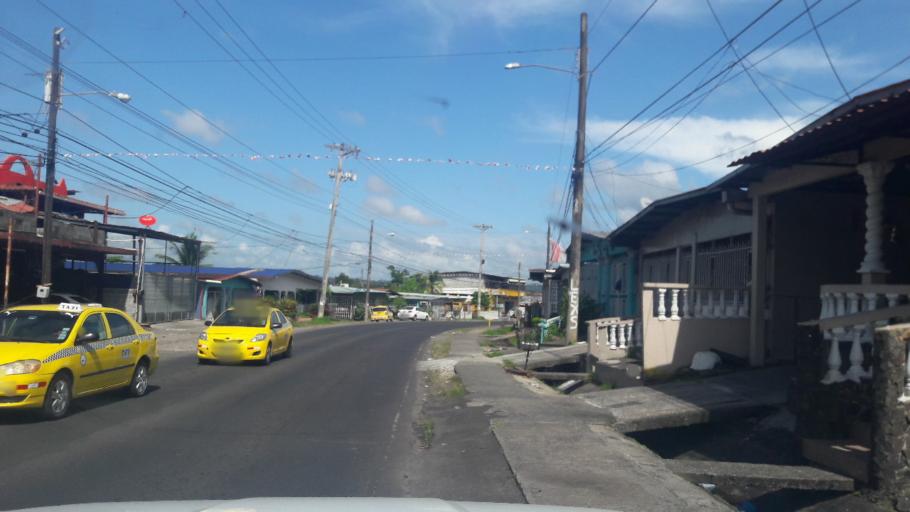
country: PA
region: Panama
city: San Miguelito
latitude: 9.0746
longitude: -79.4908
